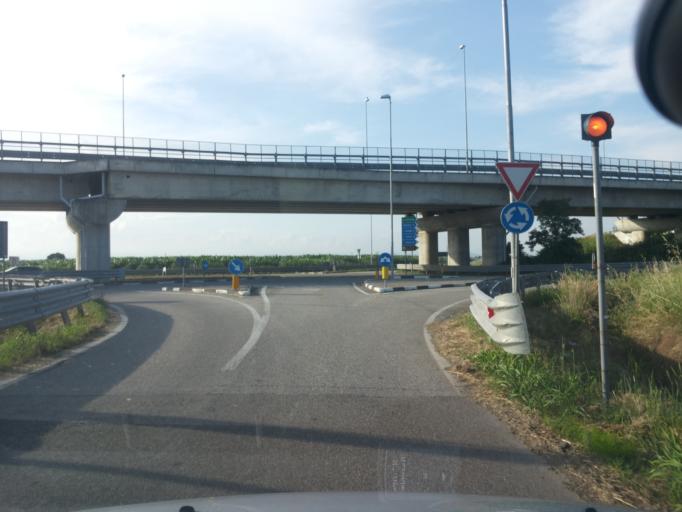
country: IT
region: Piedmont
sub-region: Provincia di Vercelli
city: Borgo Vercelli
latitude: 45.3635
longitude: 8.4607
